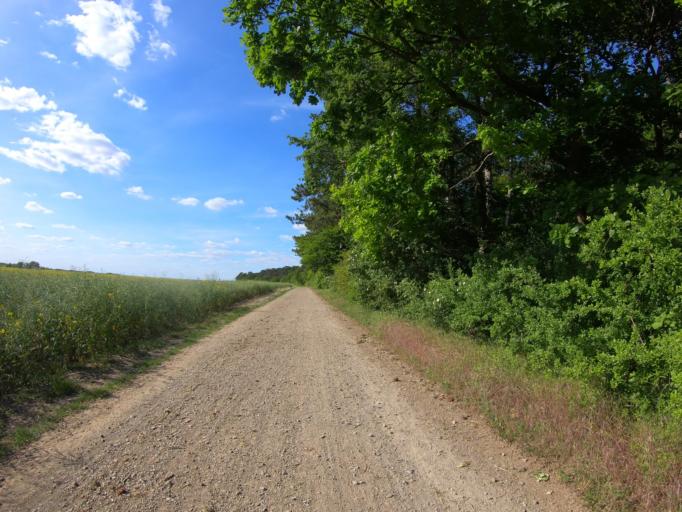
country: DE
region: Lower Saxony
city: Wolfenbuettel
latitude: 52.1865
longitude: 10.5287
